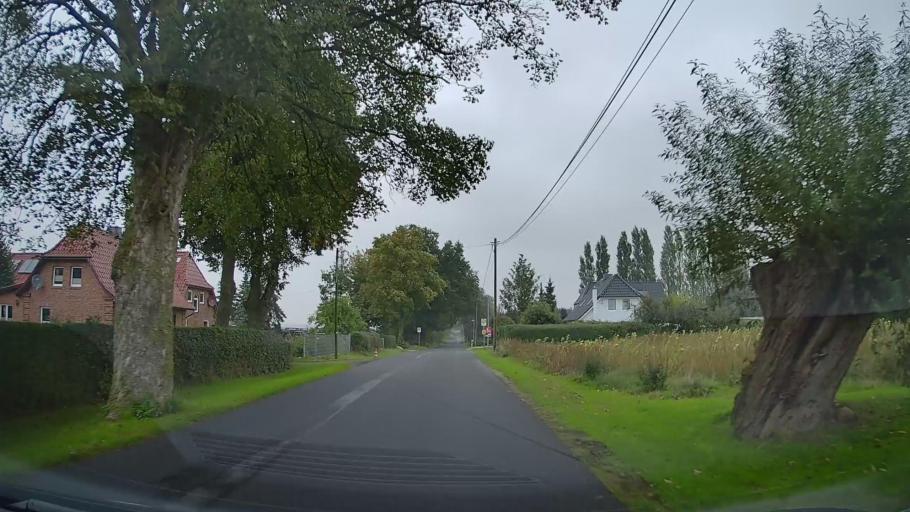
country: DE
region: Mecklenburg-Vorpommern
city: Hornstorf
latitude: 53.9226
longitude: 11.5377
